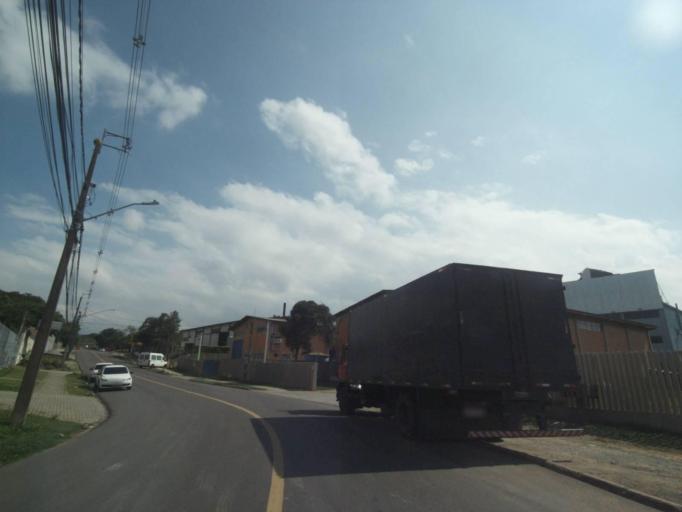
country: BR
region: Parana
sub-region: Curitiba
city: Curitiba
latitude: -25.5037
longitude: -49.3433
